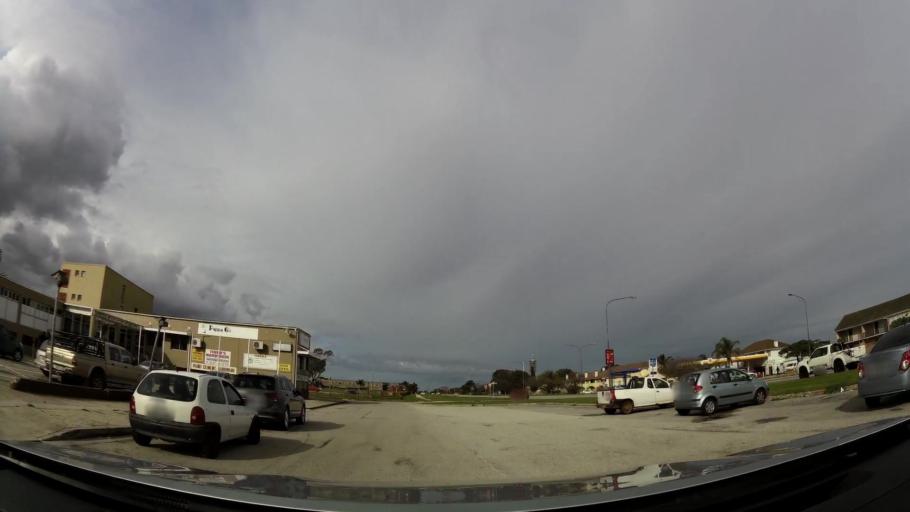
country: ZA
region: Eastern Cape
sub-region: Nelson Mandela Bay Metropolitan Municipality
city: Port Elizabeth
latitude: -33.9413
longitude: 25.5042
